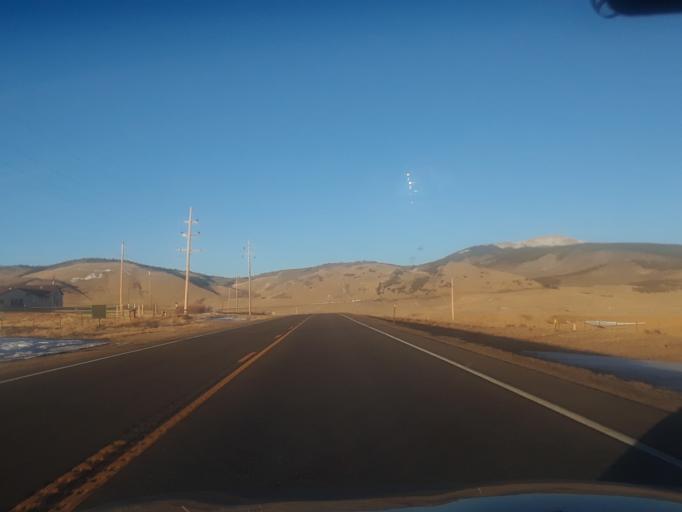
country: US
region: Colorado
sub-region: Park County
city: Fairplay
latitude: 39.3822
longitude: -105.7949
